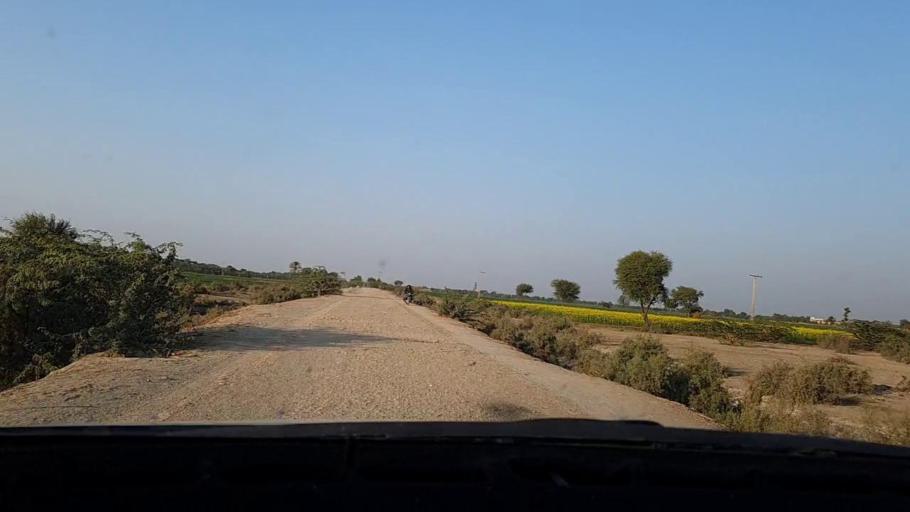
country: PK
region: Sindh
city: Tando Mittha Khan
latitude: 25.8569
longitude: 69.2725
